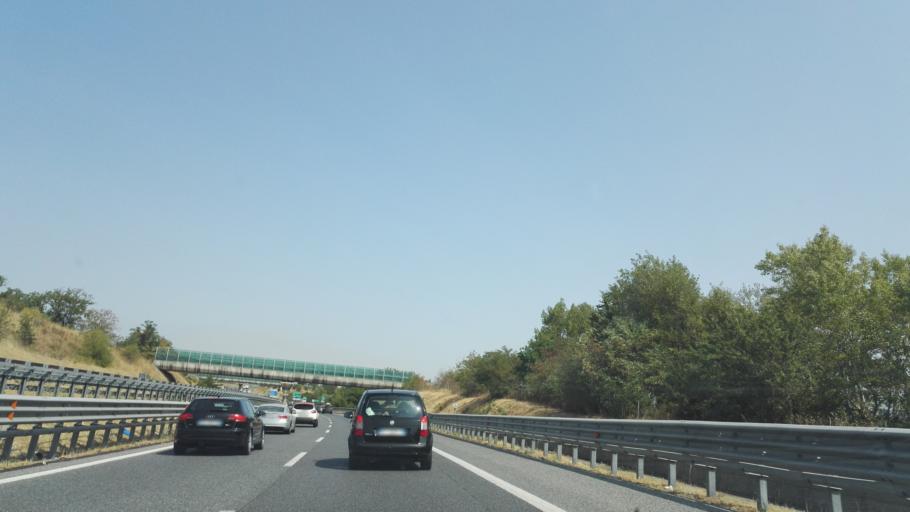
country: IT
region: Calabria
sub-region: Provincia di Cosenza
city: Stazione Montalto-Coretto
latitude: 39.4132
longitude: 16.2449
